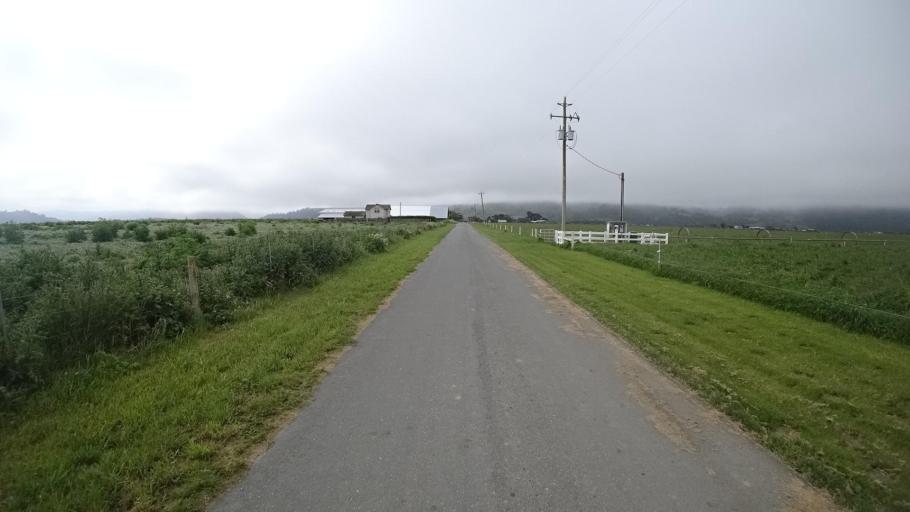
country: US
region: California
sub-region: Humboldt County
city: Fortuna
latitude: 40.5734
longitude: -124.1878
